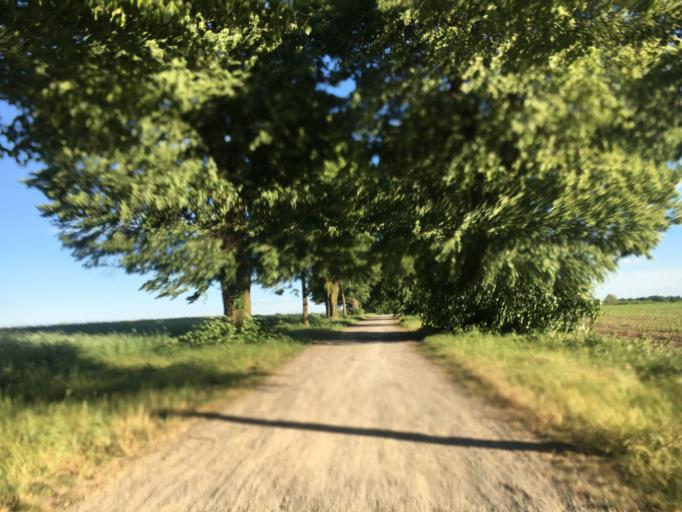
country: DE
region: Brandenburg
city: Potsdam
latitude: 52.4336
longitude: 13.0235
